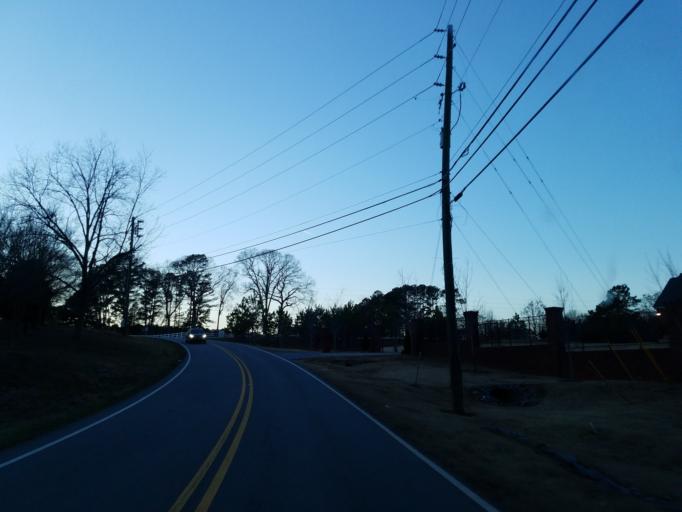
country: US
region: Georgia
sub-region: Cherokee County
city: Holly Springs
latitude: 34.1235
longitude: -84.4390
